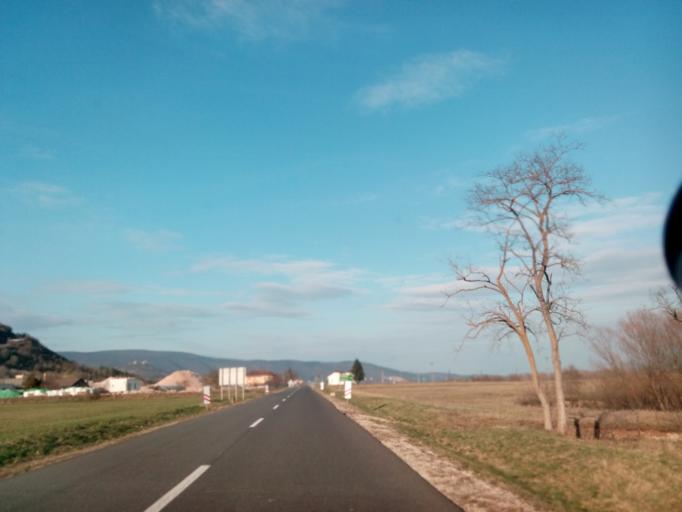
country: SK
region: Kosicky
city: Medzev
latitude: 48.5787
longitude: 20.8460
